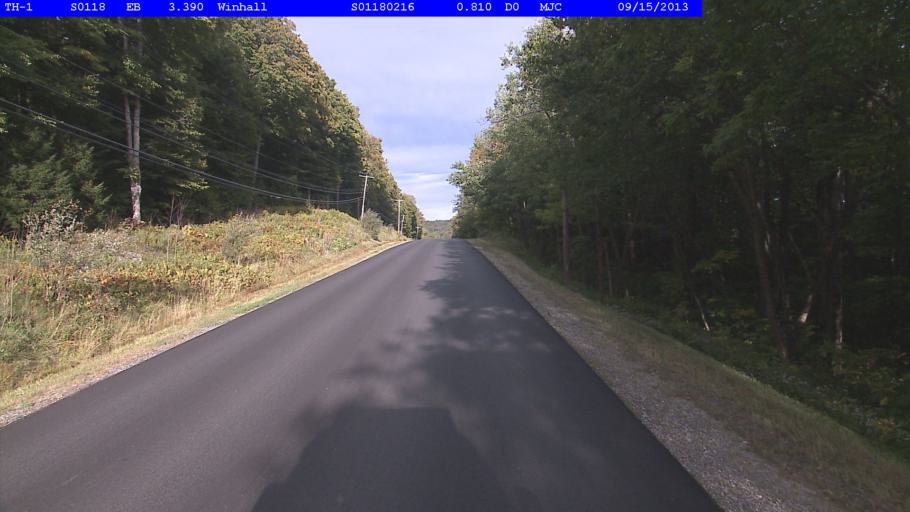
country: US
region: Vermont
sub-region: Bennington County
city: Manchester Center
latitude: 43.1254
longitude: -72.9101
